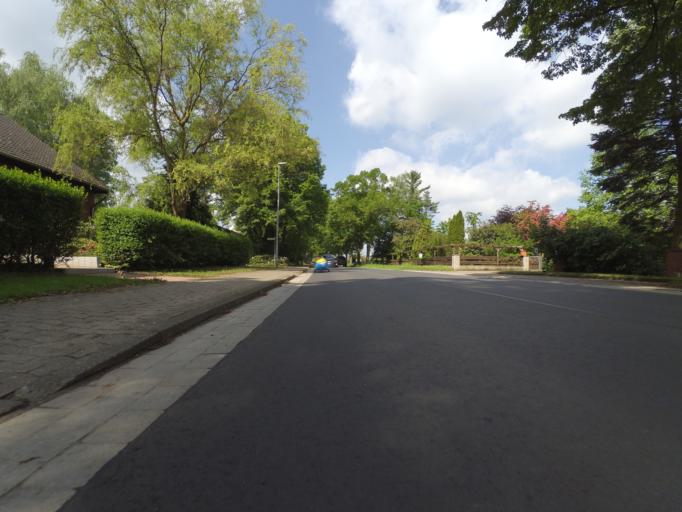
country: DE
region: Lower Saxony
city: Edemissen
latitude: 52.3862
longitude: 10.2189
